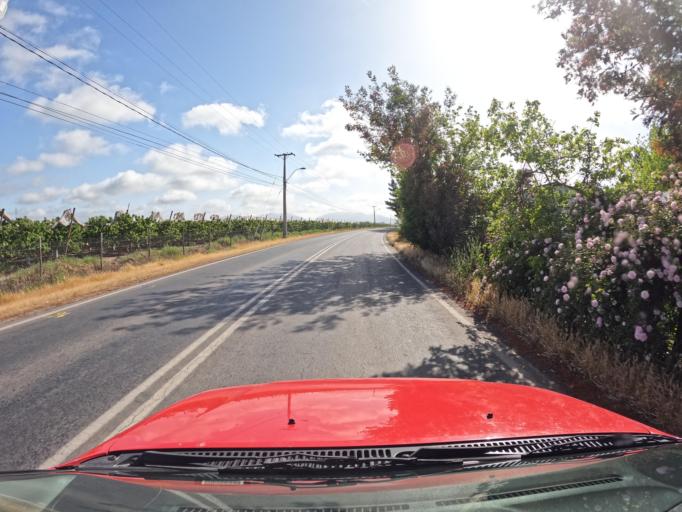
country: CL
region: Maule
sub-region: Provincia de Curico
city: Rauco
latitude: -34.9021
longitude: -71.2762
